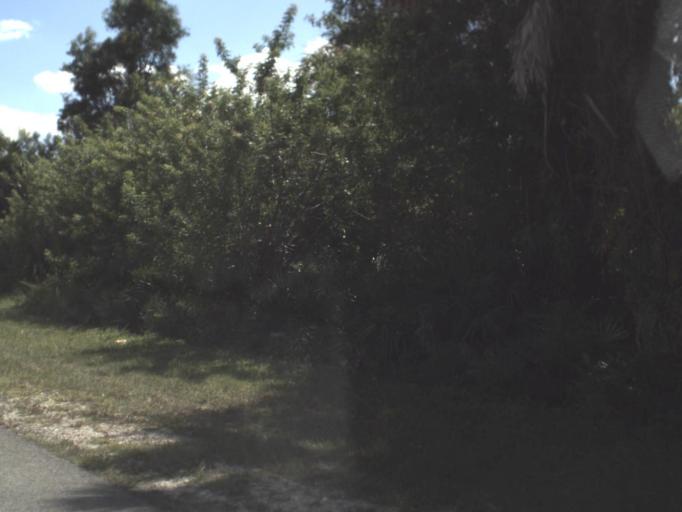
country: US
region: Florida
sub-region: Collier County
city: Lely Resort
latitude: 26.0261
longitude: -81.6411
